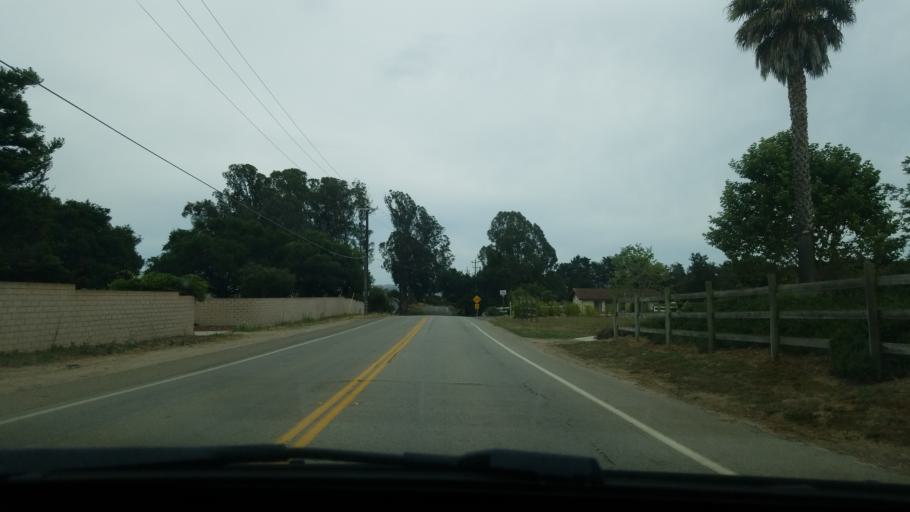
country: US
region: California
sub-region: San Luis Obispo County
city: Nipomo
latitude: 35.0114
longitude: -120.4942
